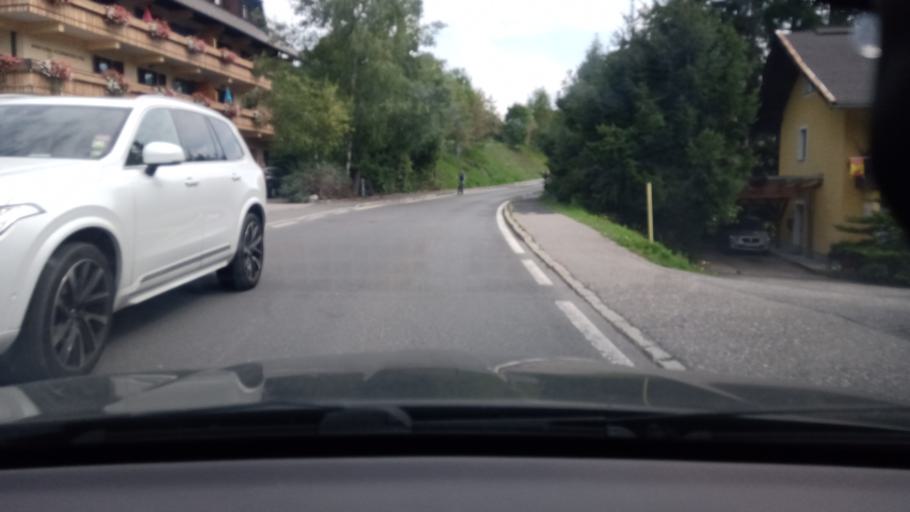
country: AT
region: Carinthia
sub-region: Politischer Bezirk Spittal an der Drau
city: Steinfeld
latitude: 46.7199
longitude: 13.2830
